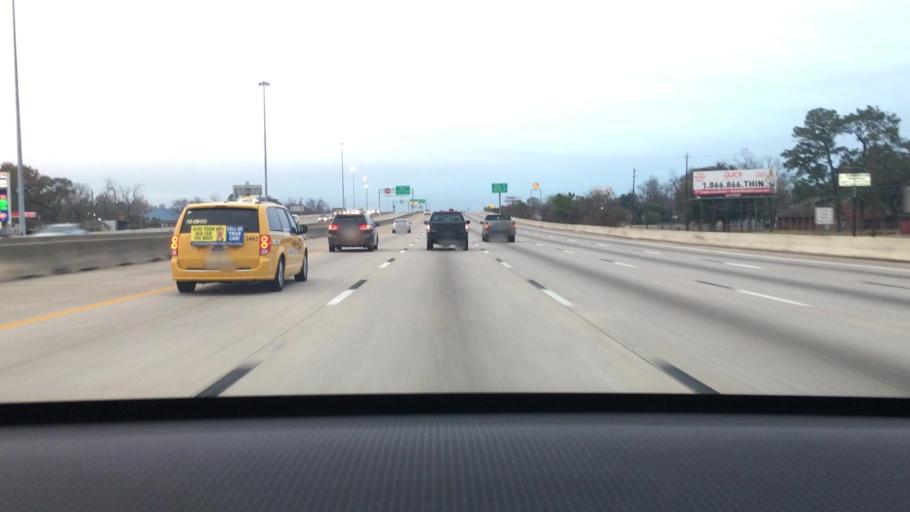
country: US
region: Texas
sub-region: Harris County
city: Houston
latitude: 29.8441
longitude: -95.3334
